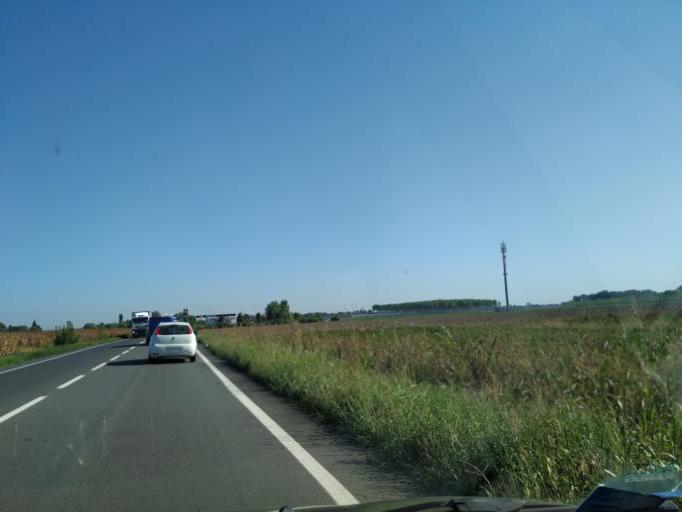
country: IT
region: Emilia-Romagna
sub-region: Provincia di Bologna
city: Decima
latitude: 44.7094
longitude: 11.2416
